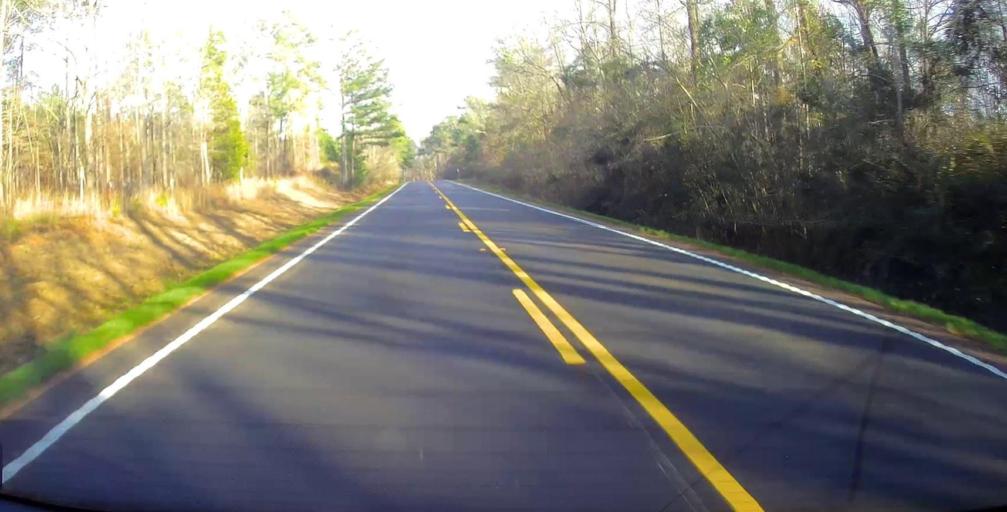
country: US
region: Georgia
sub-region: Harris County
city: Hamilton
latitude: 32.7485
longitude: -84.9170
